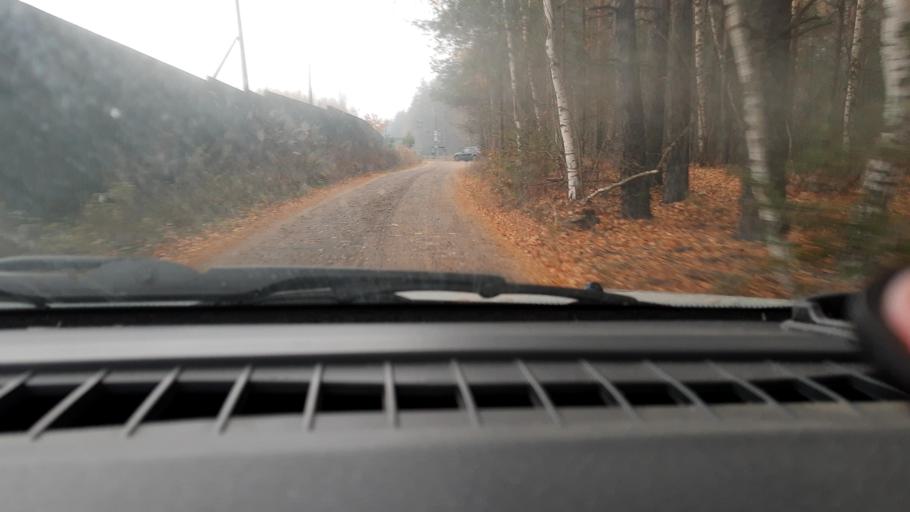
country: RU
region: Nizjnij Novgorod
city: Sitniki
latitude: 56.4251
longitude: 44.0539
